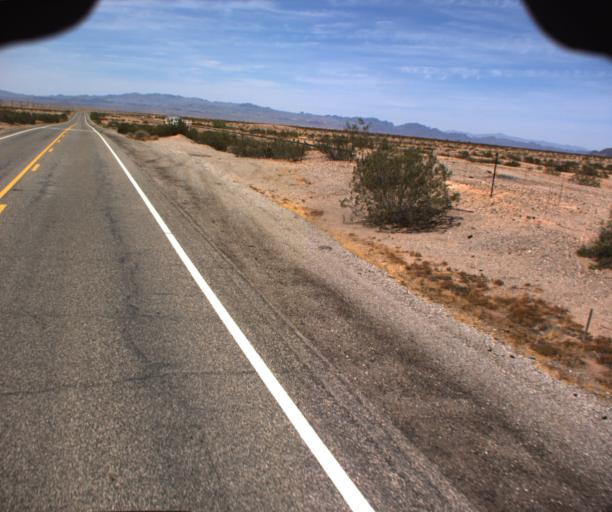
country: US
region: Arizona
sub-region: La Paz County
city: Parker
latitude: 34.0231
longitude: -114.2520
